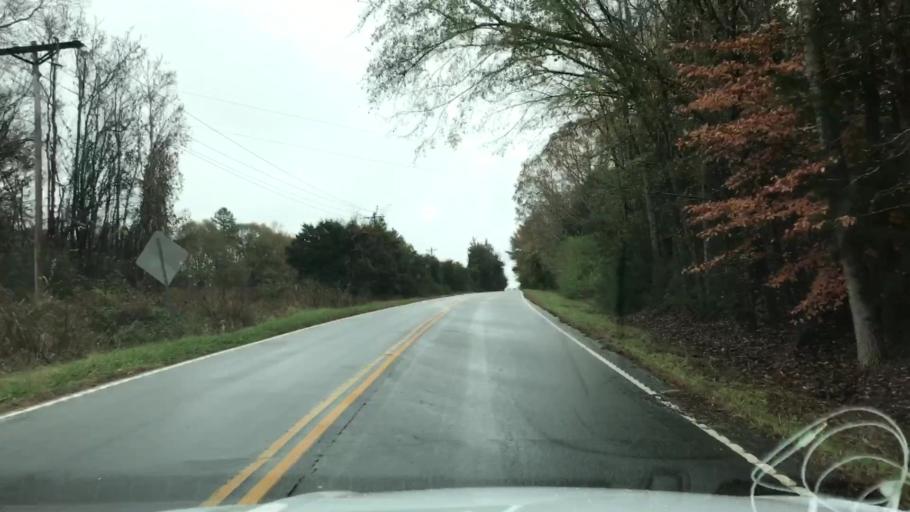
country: US
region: South Carolina
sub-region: Spartanburg County
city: Woodruff
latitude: 34.7576
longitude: -81.9242
